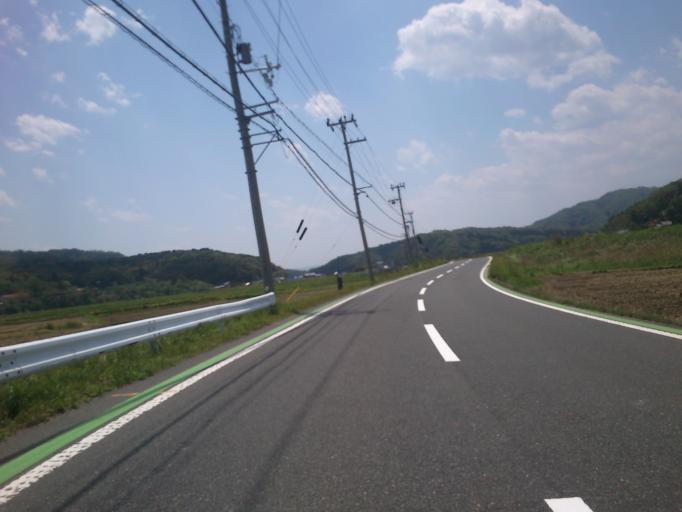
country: JP
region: Kyoto
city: Miyazu
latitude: 35.7178
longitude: 135.1081
